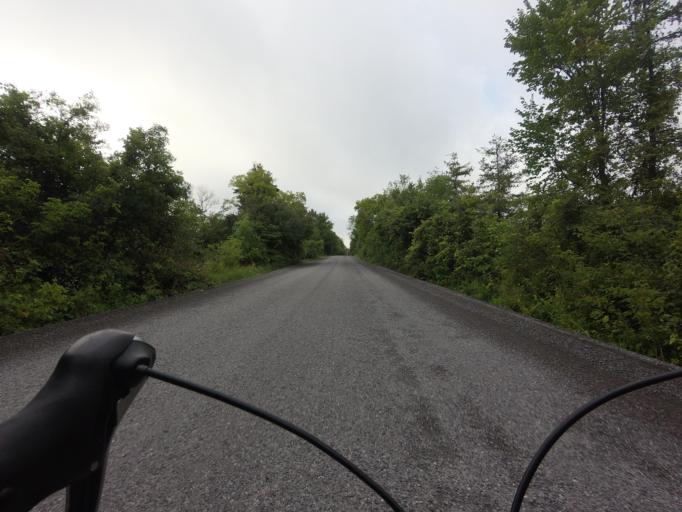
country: CA
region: Ontario
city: Bells Corners
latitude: 45.0793
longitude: -75.7572
